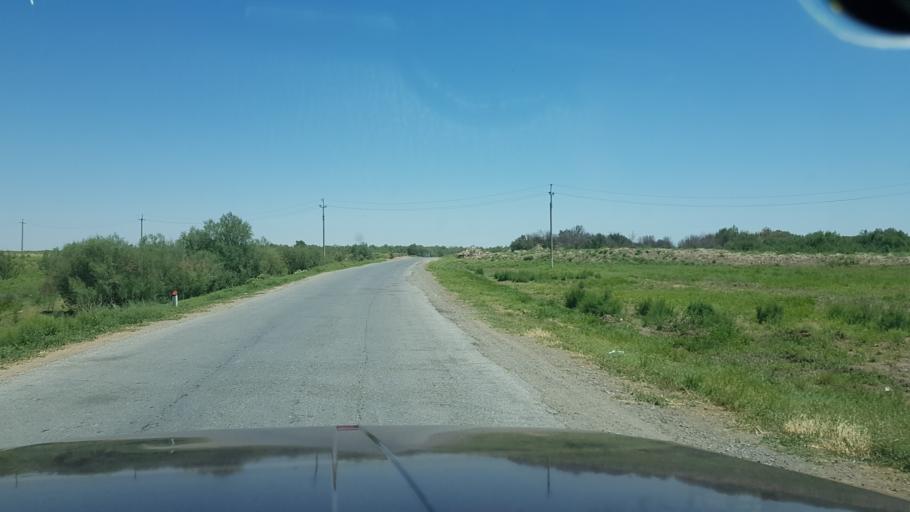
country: TM
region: Ahal
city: Annau
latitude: 37.8848
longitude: 58.7334
